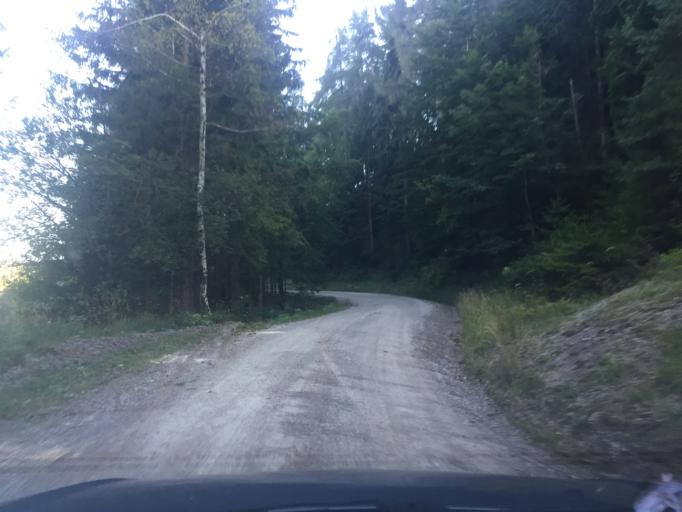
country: SI
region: Ravne na Koroskem
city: Kotlje
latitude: 46.4676
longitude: 14.9886
